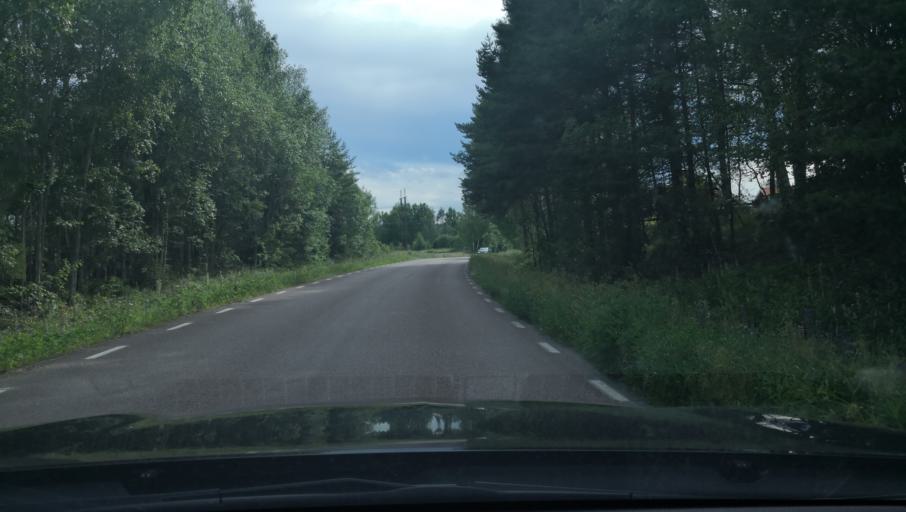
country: SE
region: Dalarna
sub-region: Smedjebackens Kommun
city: Smedjebacken
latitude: 60.0483
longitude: 15.5499
